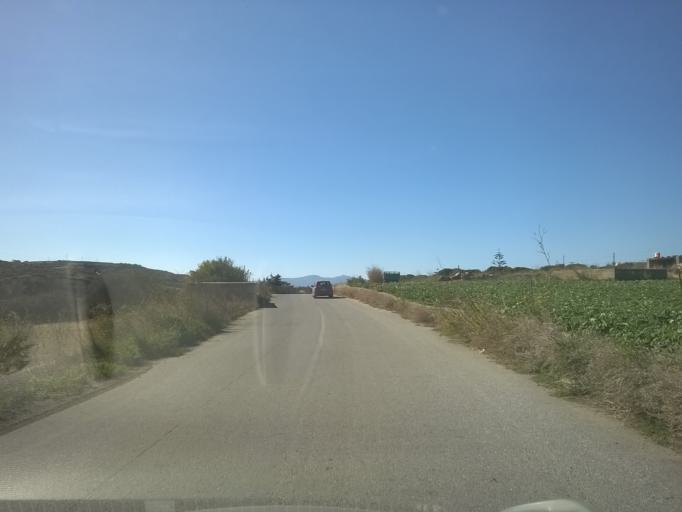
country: GR
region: South Aegean
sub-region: Nomos Kykladon
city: Naxos
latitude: 37.0436
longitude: 25.4122
